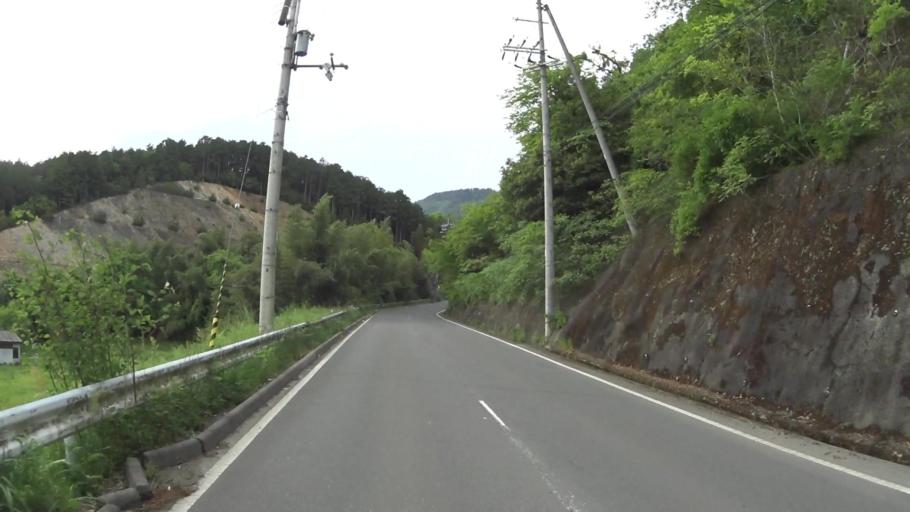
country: JP
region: Kyoto
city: Kameoka
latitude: 35.0983
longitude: 135.5431
